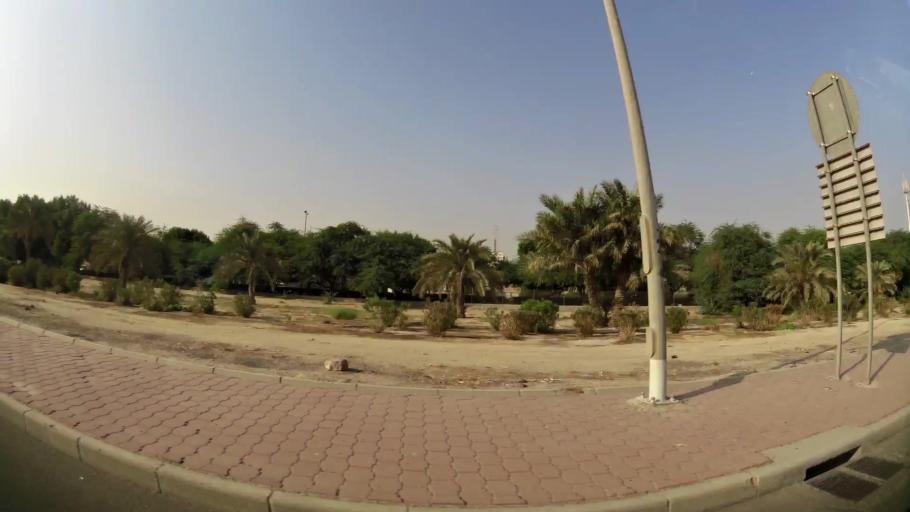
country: KW
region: Muhafazat Hawalli
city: Salwa
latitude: 29.2811
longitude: 48.0774
